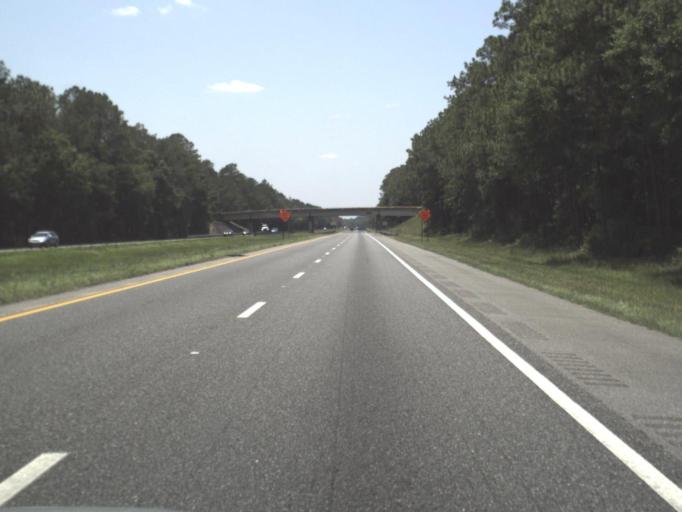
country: US
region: Florida
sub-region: Columbia County
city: Watertown
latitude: 30.2519
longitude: -82.5117
